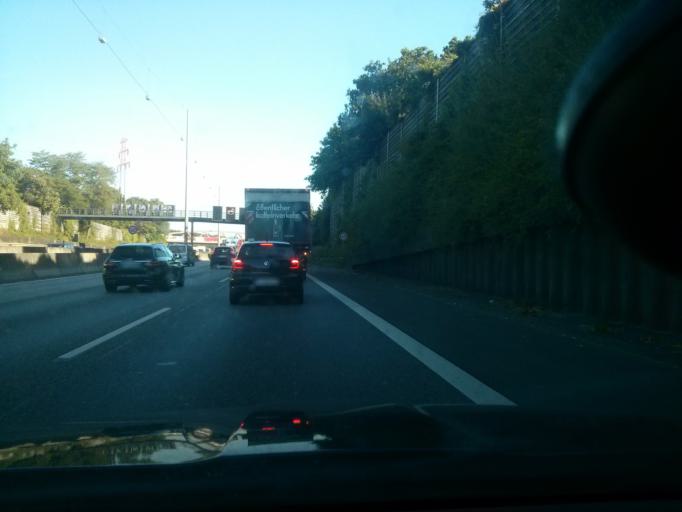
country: DE
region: Hamburg
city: Stellingen
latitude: 53.6016
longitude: 9.9222
